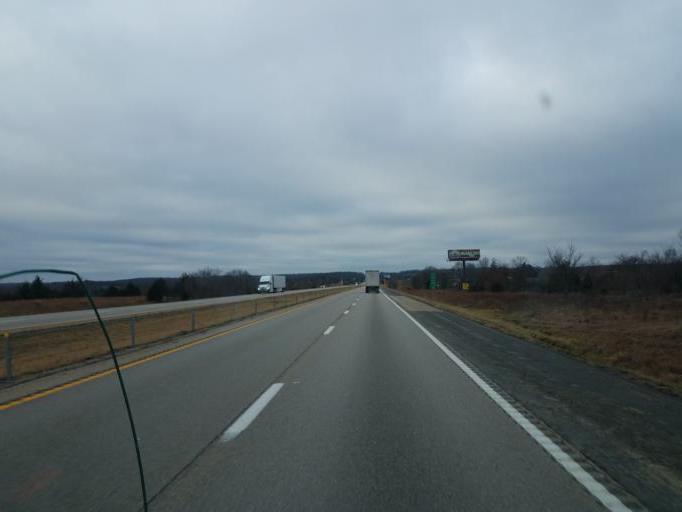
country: US
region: Missouri
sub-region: Laclede County
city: Lebanon
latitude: 37.5796
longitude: -92.7523
